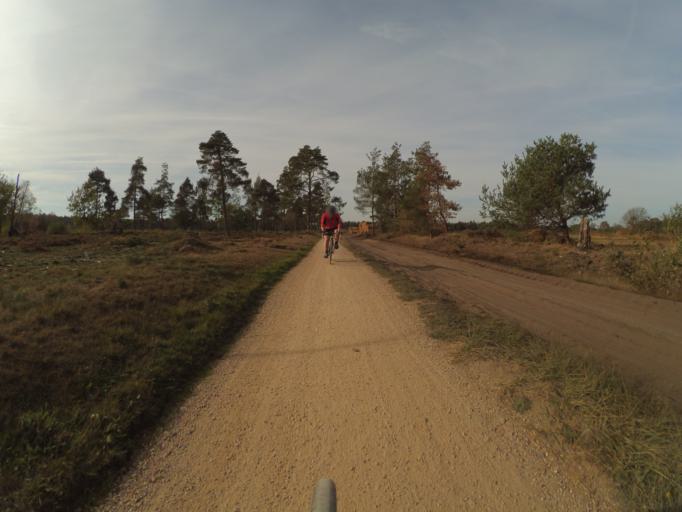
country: NL
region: Overijssel
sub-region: Gemeente Twenterand
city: Den Ham
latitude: 52.3623
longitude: 6.4175
